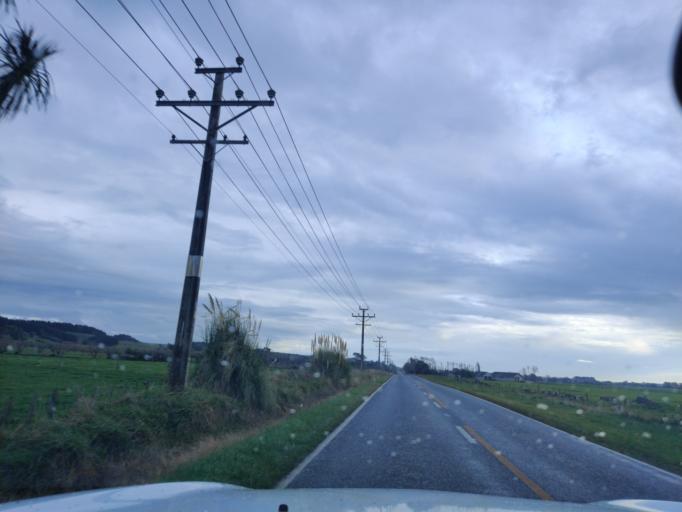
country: NZ
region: Manawatu-Wanganui
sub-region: Palmerston North City
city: Palmerston North
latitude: -40.3448
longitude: 175.7096
